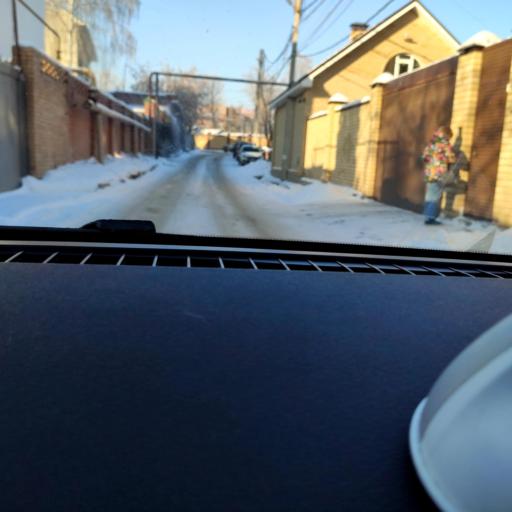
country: RU
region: Samara
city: Samara
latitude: 53.2546
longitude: 50.1846
